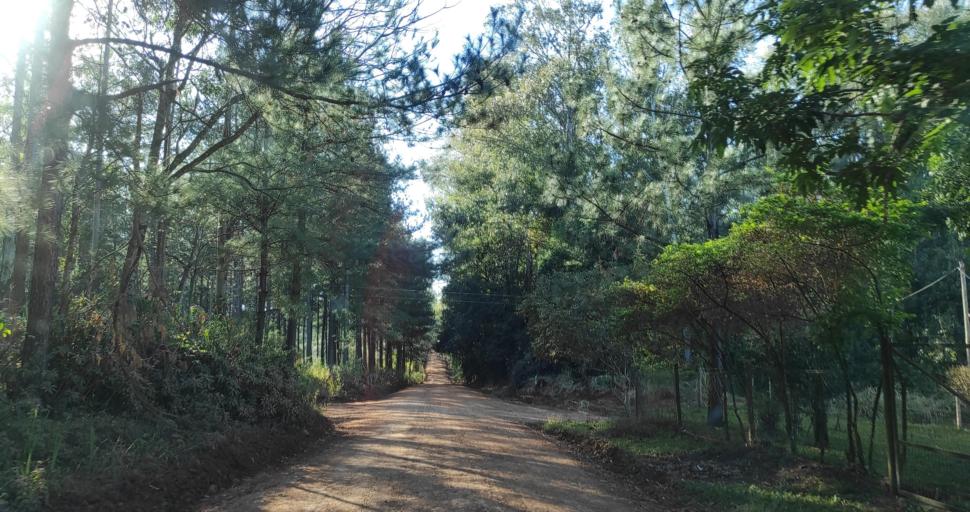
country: AR
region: Misiones
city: Capiovi
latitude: -26.8801
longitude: -55.0483
